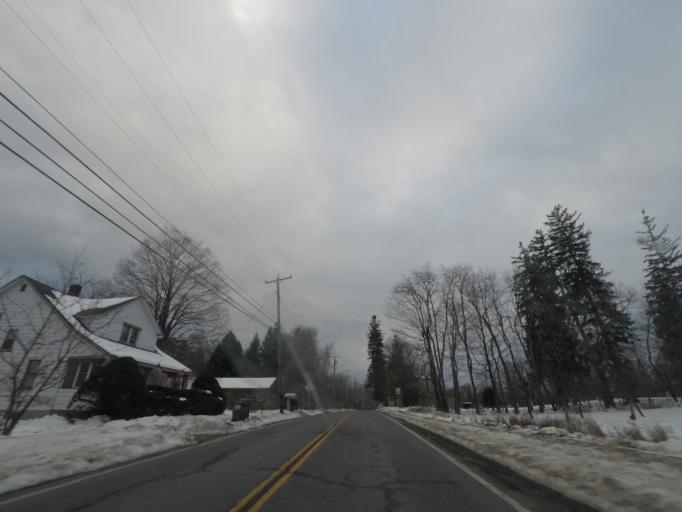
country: US
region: New York
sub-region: Ulster County
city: Clintondale
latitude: 41.6750
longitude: -74.1036
